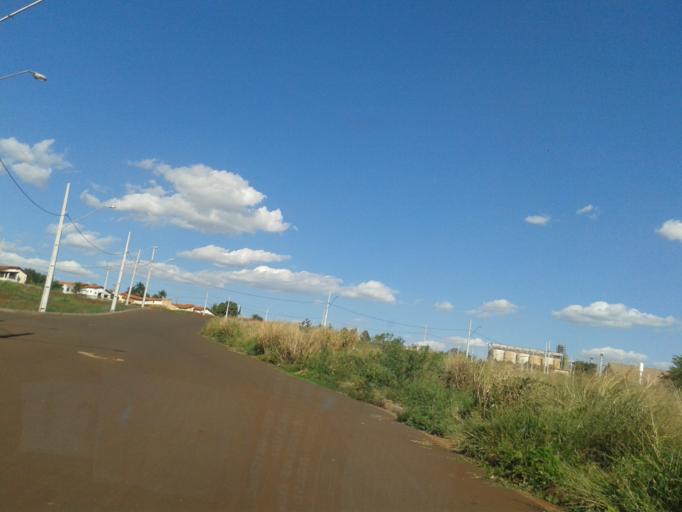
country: BR
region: Minas Gerais
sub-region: Capinopolis
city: Capinopolis
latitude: -18.6896
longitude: -49.5708
